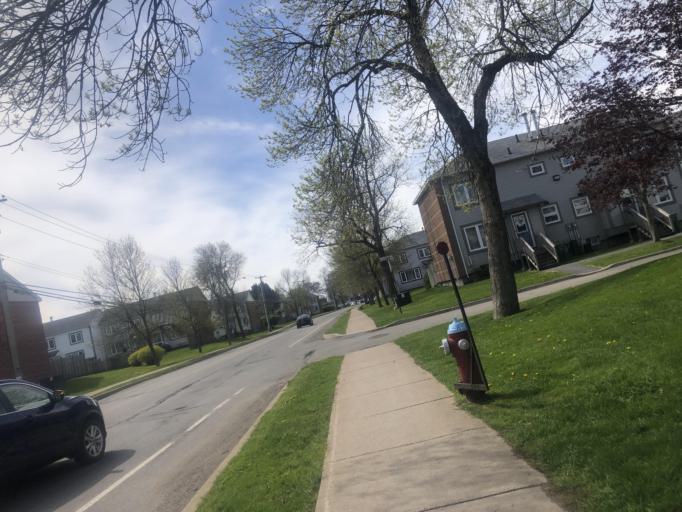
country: CA
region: New Brunswick
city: Saint John
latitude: 45.2822
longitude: -66.0782
